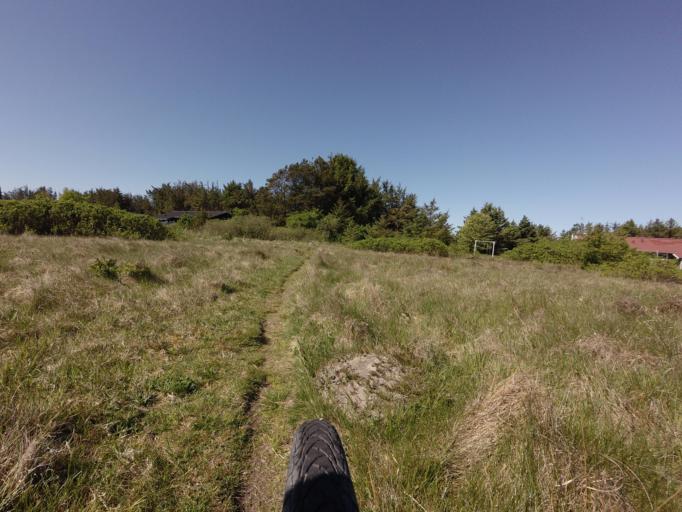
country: DK
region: North Denmark
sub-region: Jammerbugt Kommune
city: Pandrup
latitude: 57.3173
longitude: 9.6666
